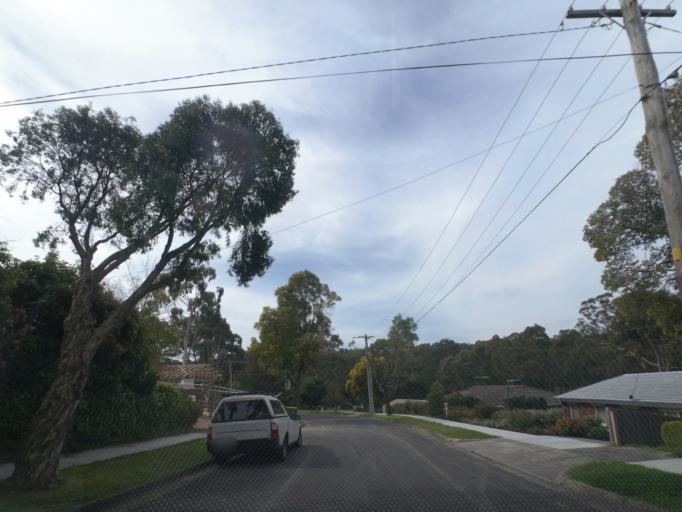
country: AU
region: Victoria
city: Mitcham
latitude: -37.8103
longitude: 145.2084
